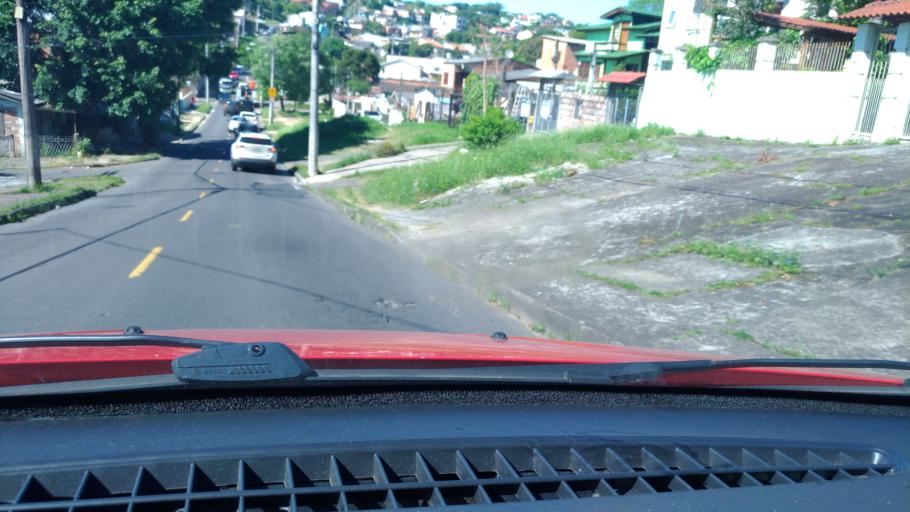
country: BR
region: Rio Grande do Sul
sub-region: Porto Alegre
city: Porto Alegre
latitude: -30.0304
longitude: -51.1477
